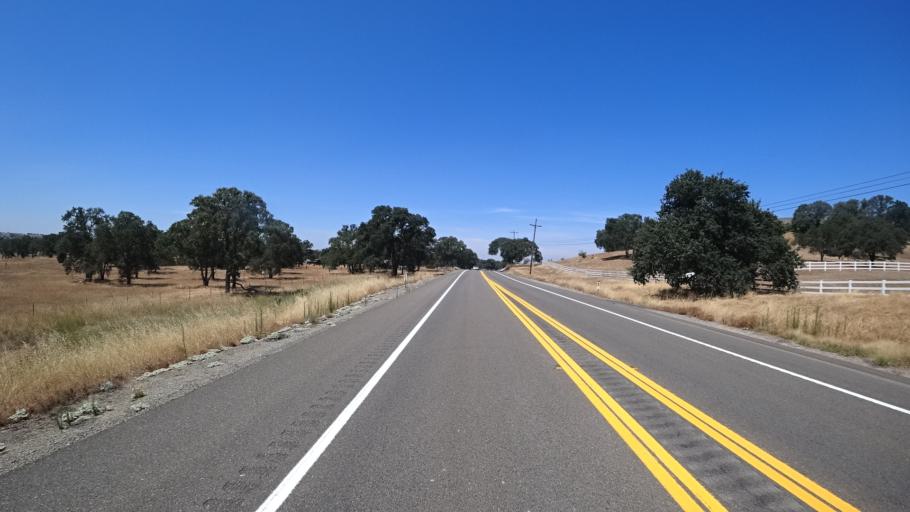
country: US
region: California
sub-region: Calaveras County
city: Rancho Calaveras
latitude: 38.1788
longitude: -120.9195
